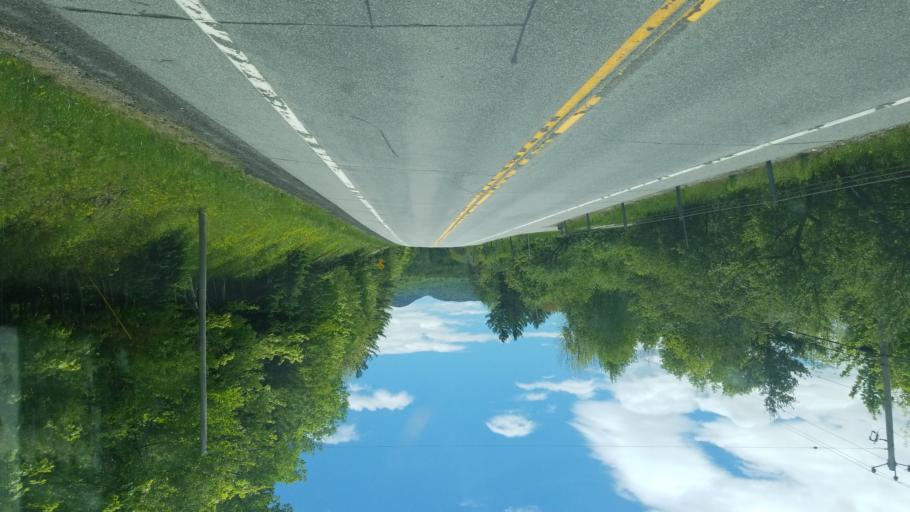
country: US
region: New York
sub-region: Hamilton County
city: Lake Pleasant
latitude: 43.7676
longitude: -74.2717
